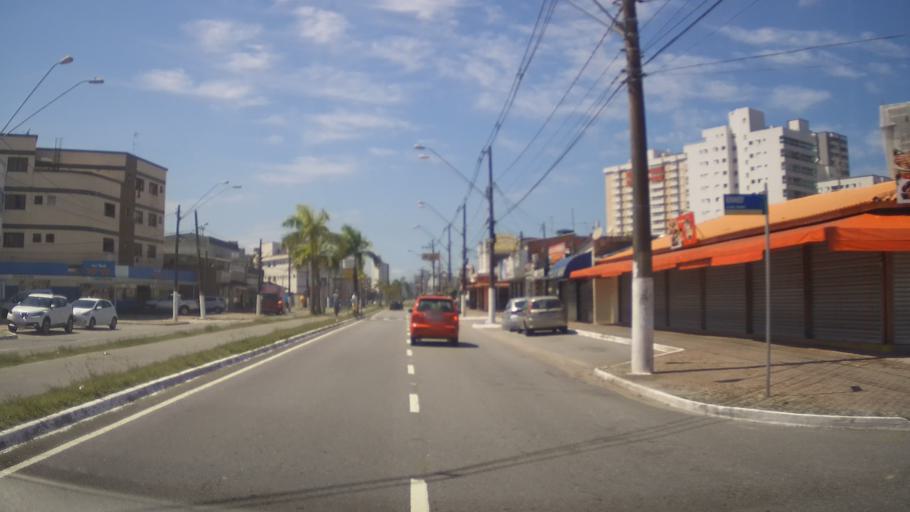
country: BR
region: Sao Paulo
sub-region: Praia Grande
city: Praia Grande
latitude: -24.0246
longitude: -46.4760
